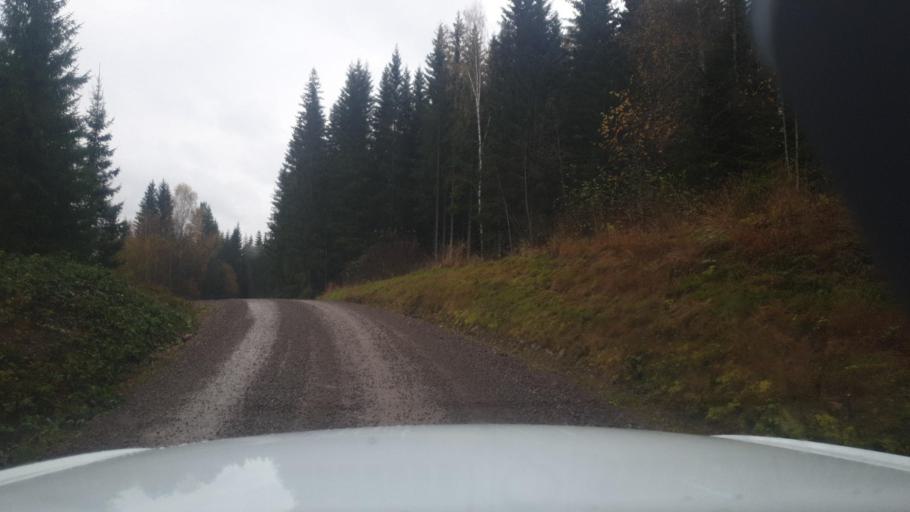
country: SE
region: Vaermland
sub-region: Eda Kommun
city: Charlottenberg
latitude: 60.0328
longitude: 12.5975
